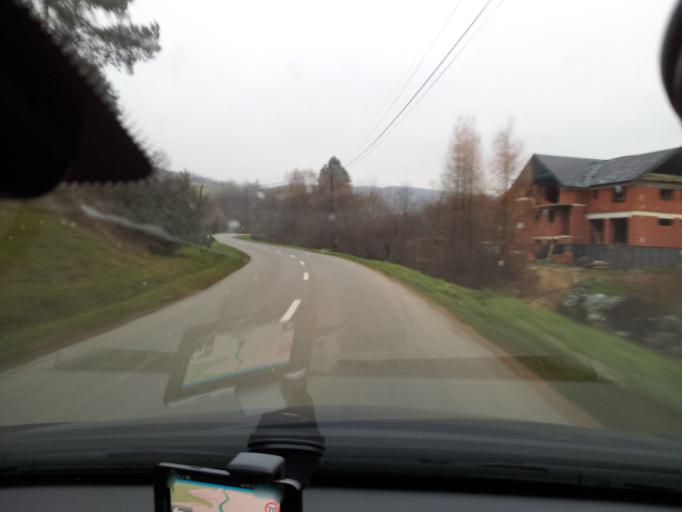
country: SK
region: Presovsky
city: Giraltovce
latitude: 49.0588
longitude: 21.5872
